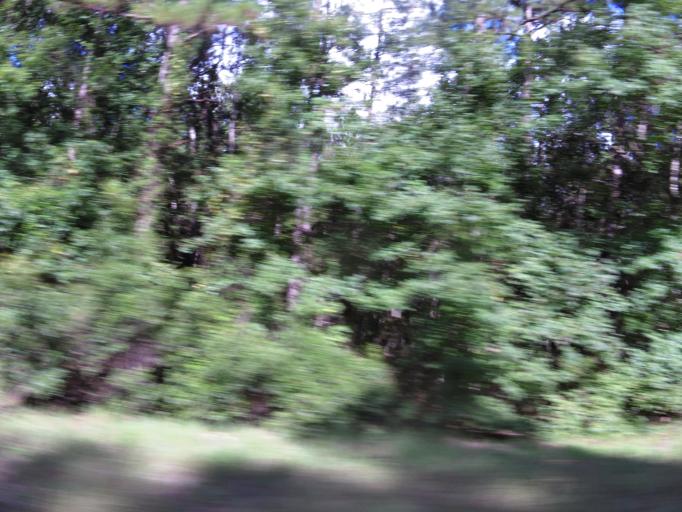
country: US
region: Georgia
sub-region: Camden County
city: Woodbine
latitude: 30.9003
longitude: -81.7099
